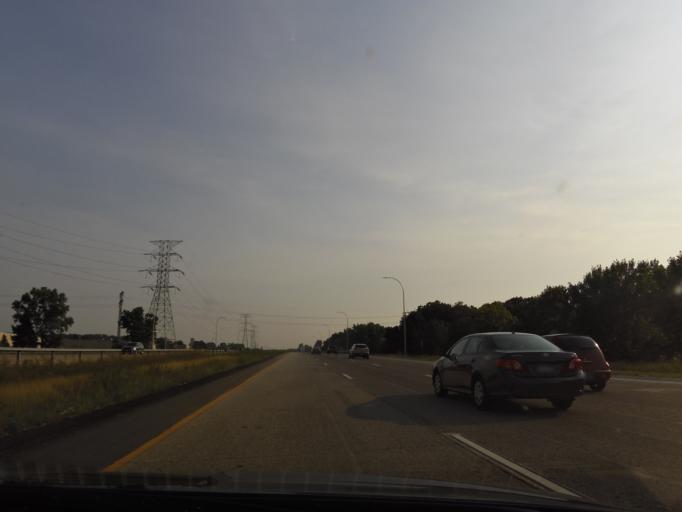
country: US
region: Minnesota
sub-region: Hennepin County
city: Plymouth
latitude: 44.9928
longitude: -93.4589
